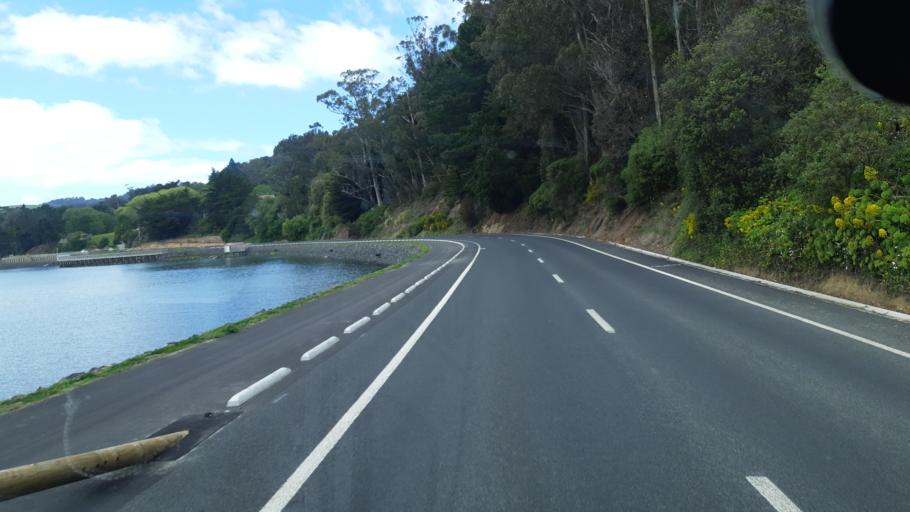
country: NZ
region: Otago
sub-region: Dunedin City
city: Dunedin
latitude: -45.8793
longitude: 170.5717
